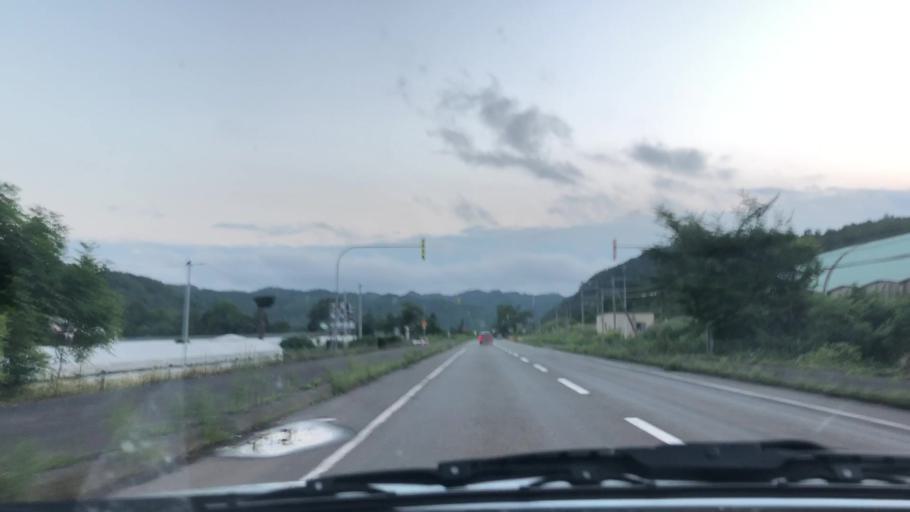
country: JP
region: Hokkaido
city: Chitose
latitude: 42.9152
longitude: 142.0256
